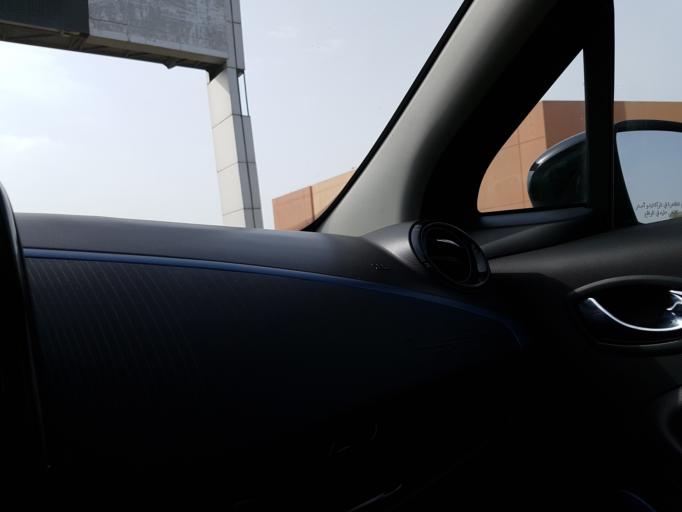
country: OM
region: Al Batinah
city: Al Sohar
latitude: 24.3908
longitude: 56.6957
